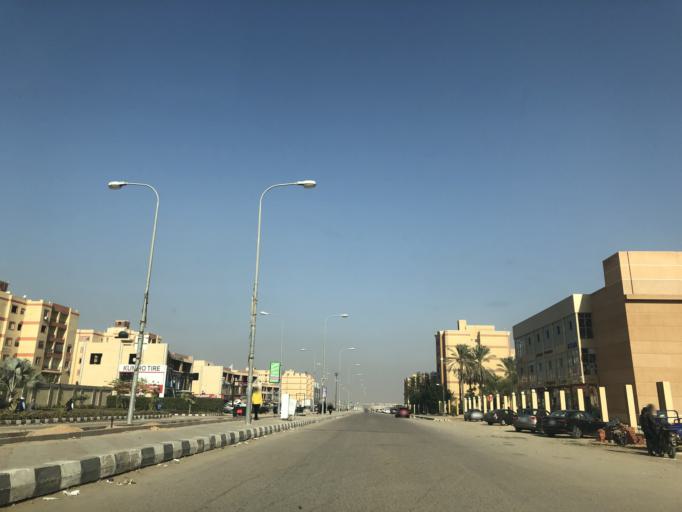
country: EG
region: Al Jizah
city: Madinat Sittah Uktubar
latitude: 29.9119
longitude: 31.0593
